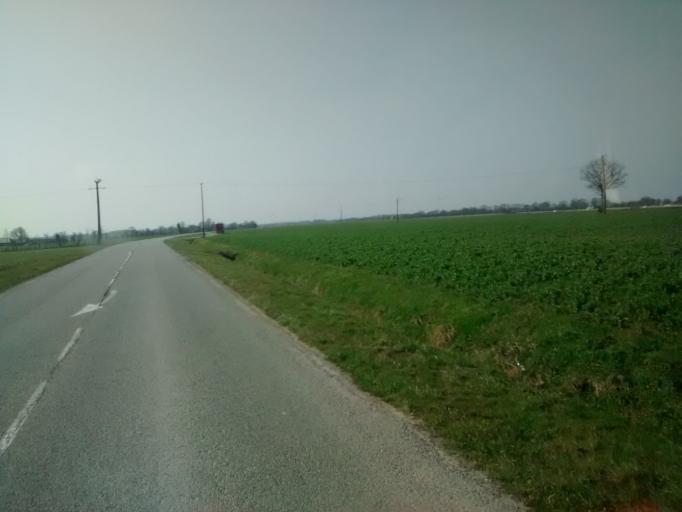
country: FR
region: Brittany
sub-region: Departement d'Ille-et-Vilaine
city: Maxent
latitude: 48.0271
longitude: -2.0174
